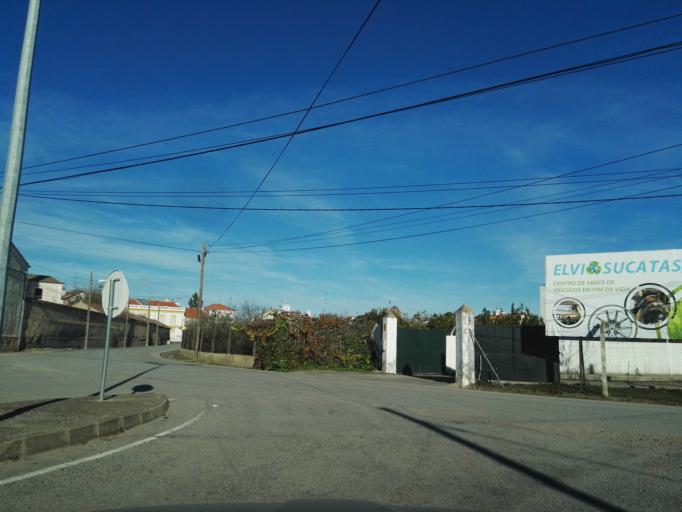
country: PT
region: Portalegre
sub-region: Elvas
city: Elvas
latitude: 38.8939
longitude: -7.1435
